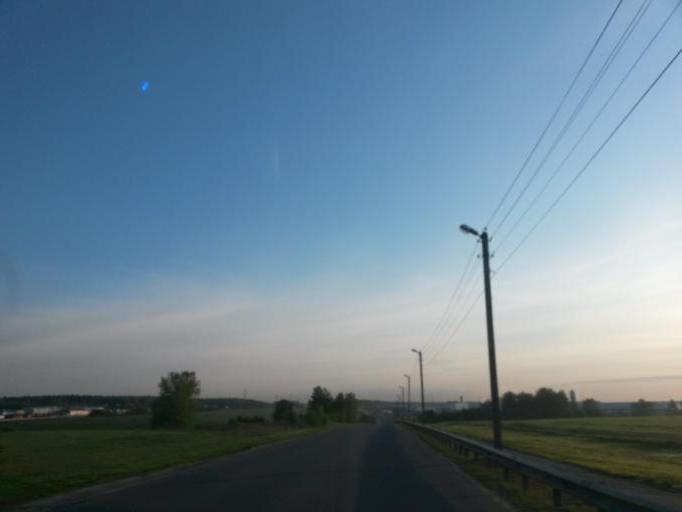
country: RU
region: Moskovskaya
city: Lyubuchany
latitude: 55.2469
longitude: 37.5322
